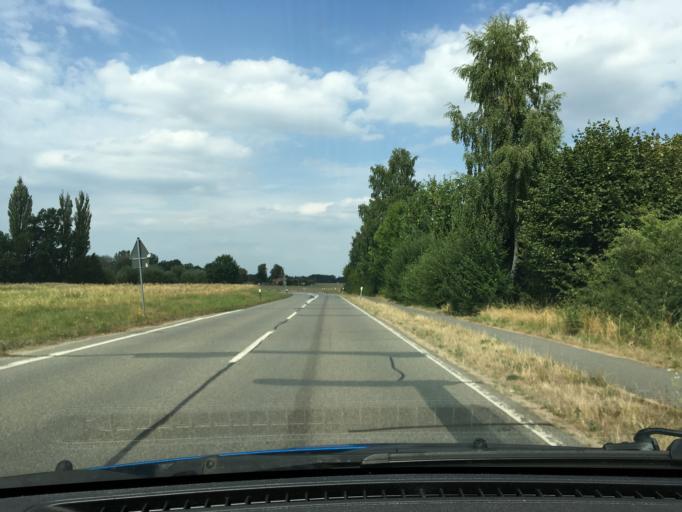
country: DE
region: Lower Saxony
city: Wendisch Evern
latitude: 53.2189
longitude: 10.4638
